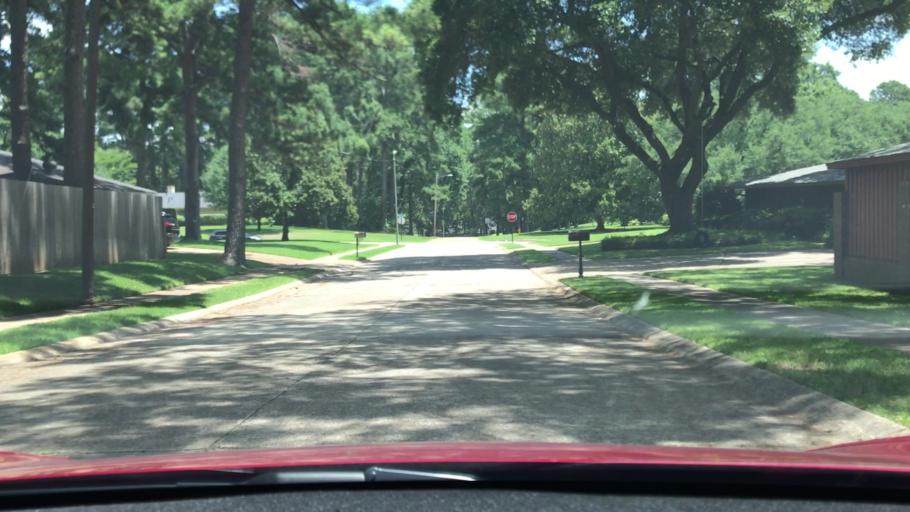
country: US
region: Louisiana
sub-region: Bossier Parish
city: Bossier City
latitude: 32.4321
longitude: -93.7342
